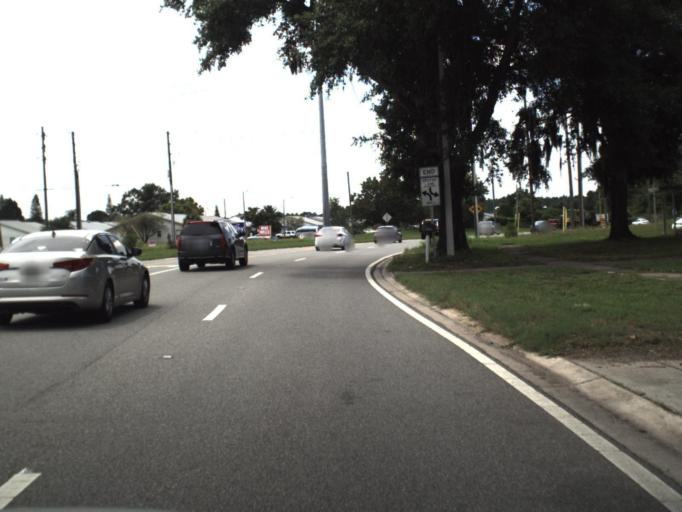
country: US
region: Florida
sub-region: Pasco County
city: Trinity
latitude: 28.2042
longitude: -82.6943
